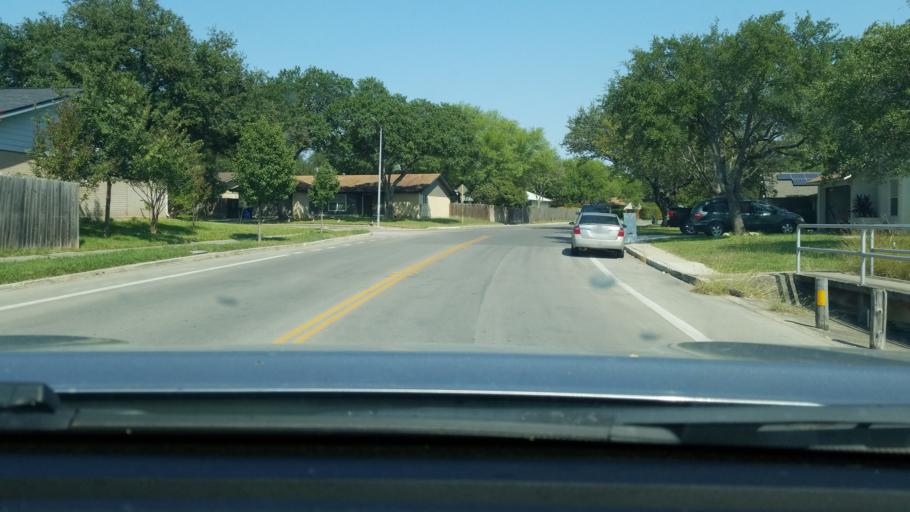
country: US
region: Texas
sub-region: Bexar County
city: Leon Valley
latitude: 29.5541
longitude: -98.6110
